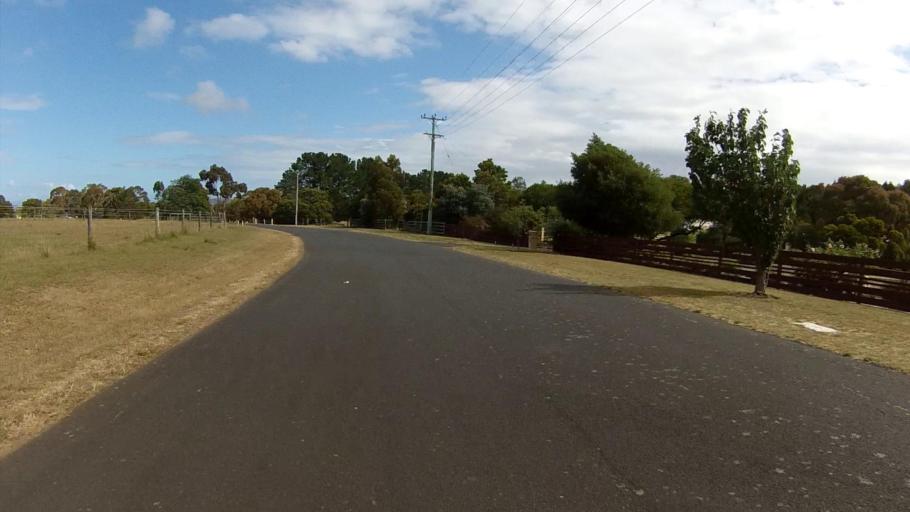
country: AU
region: Tasmania
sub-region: Clarence
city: Acton Park
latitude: -42.8834
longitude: 147.4910
